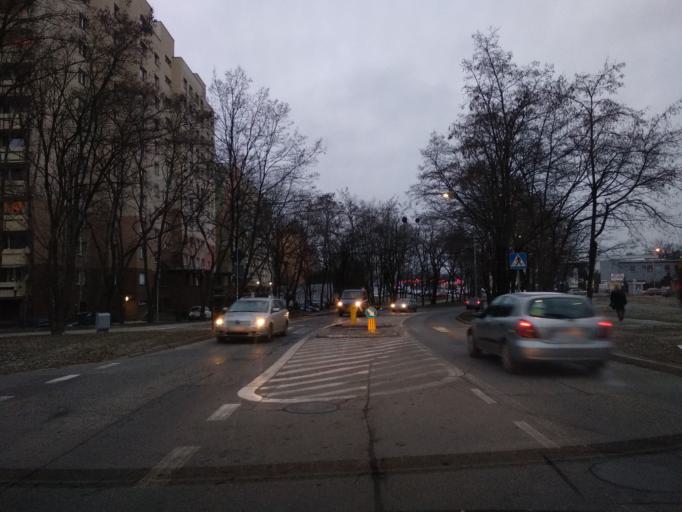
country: PL
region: Lower Silesian Voivodeship
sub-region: Powiat wroclawski
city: Wroclaw
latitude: 51.1285
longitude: 16.9704
